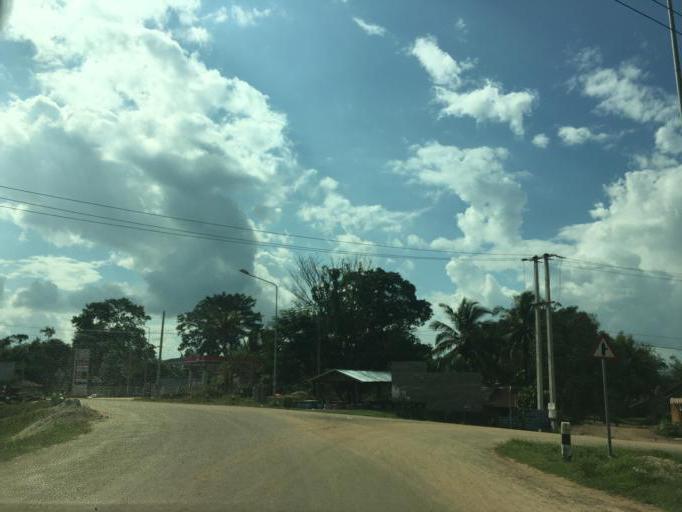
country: TH
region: Nong Khai
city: Sangkhom
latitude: 18.2200
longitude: 102.2415
